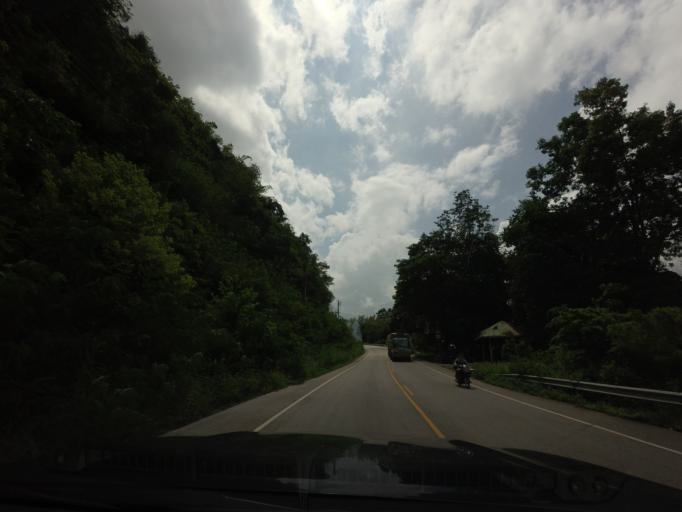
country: TH
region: Loei
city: Pak Chom
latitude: 18.0442
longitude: 101.7716
